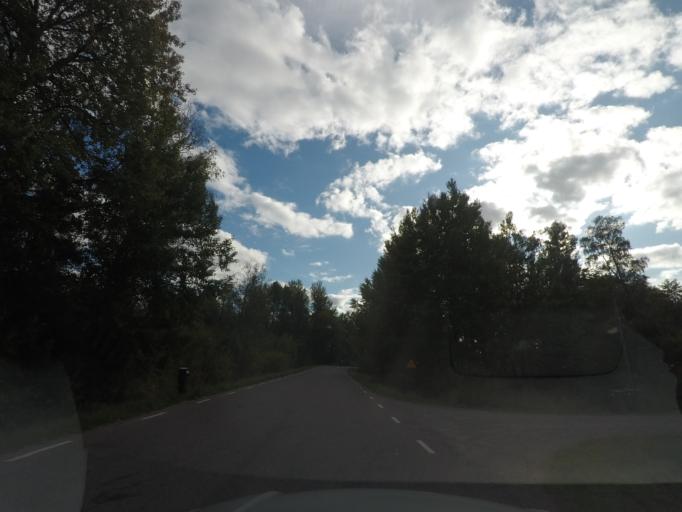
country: SE
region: Vaestmanland
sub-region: Hallstahammars Kommun
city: Kolback
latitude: 59.5219
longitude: 16.1906
